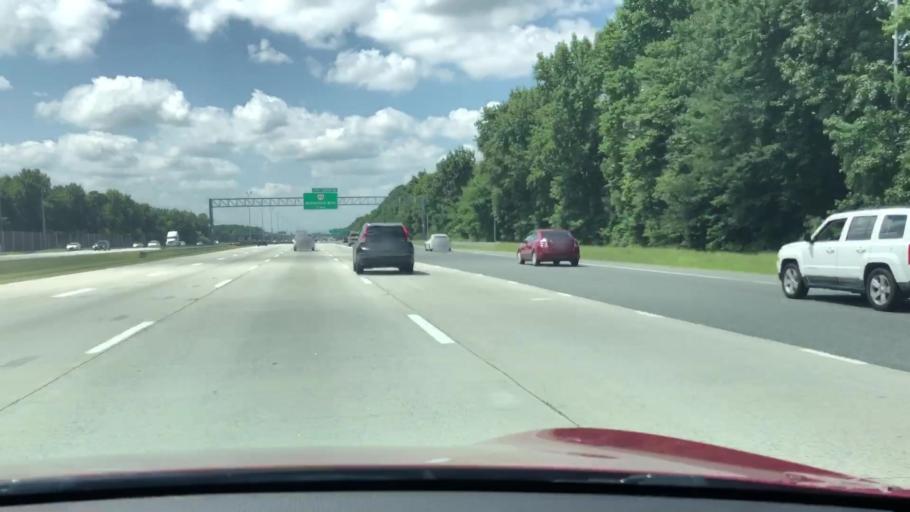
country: US
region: Virginia
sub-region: City of Chesapeake
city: Chesapeake
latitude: 36.7895
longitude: -76.2244
